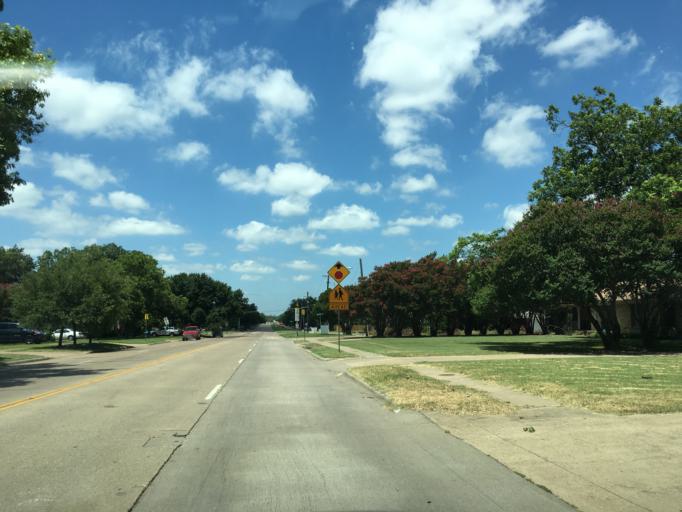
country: US
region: Texas
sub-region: Dallas County
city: Garland
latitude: 32.8429
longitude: -96.6713
